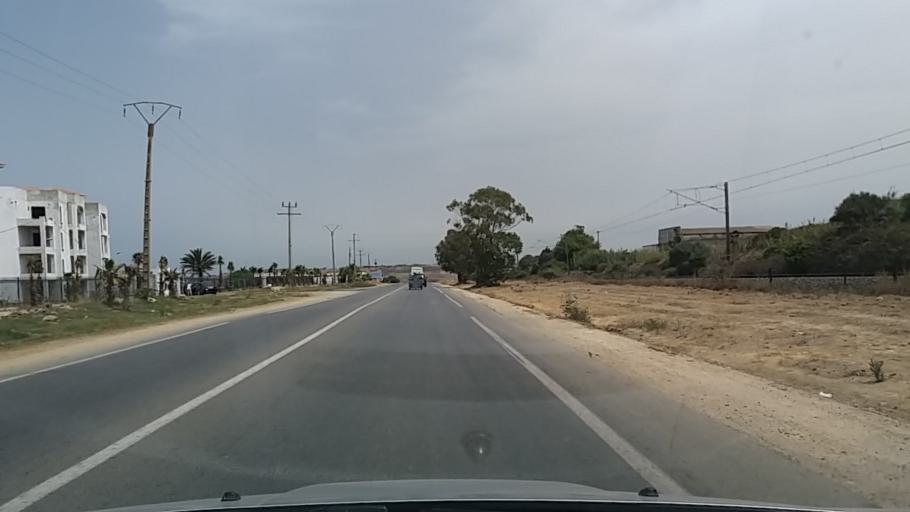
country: MA
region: Tanger-Tetouan
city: Asilah
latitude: 35.4961
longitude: -6.0149
